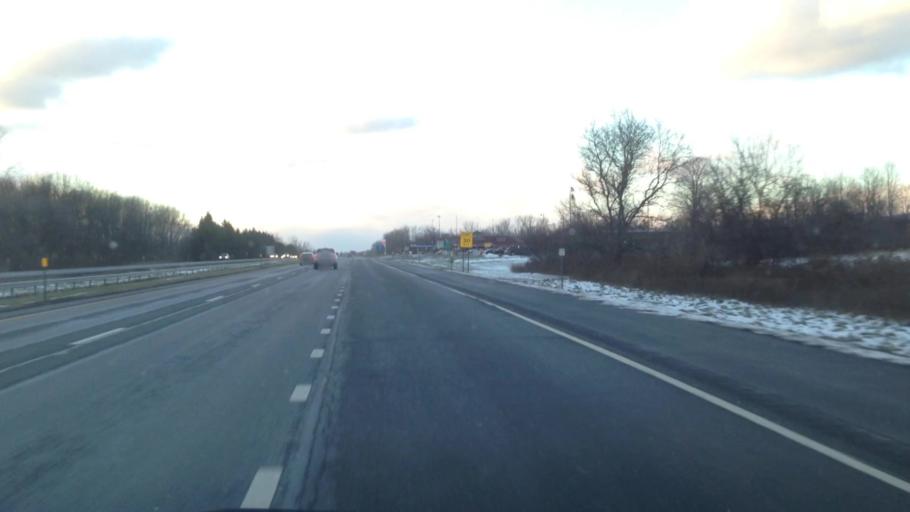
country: US
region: New York
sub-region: Herkimer County
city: Frankfort
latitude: 43.0736
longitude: -75.0991
